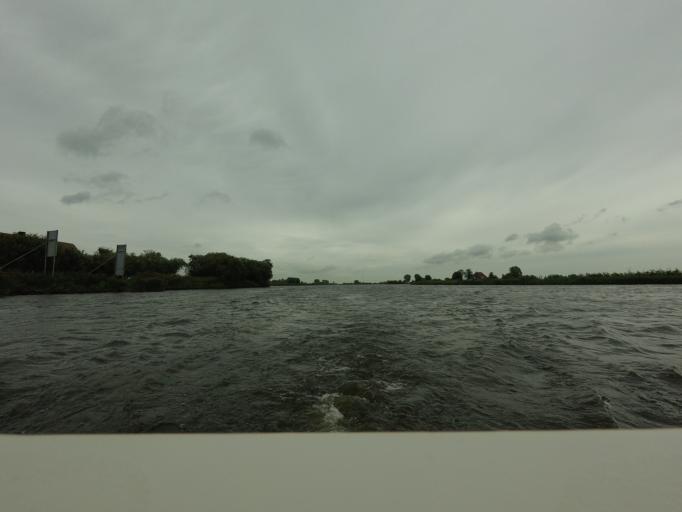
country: NL
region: Friesland
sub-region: Gemeente Boarnsterhim
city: Grou
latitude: 53.1028
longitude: 5.8519
